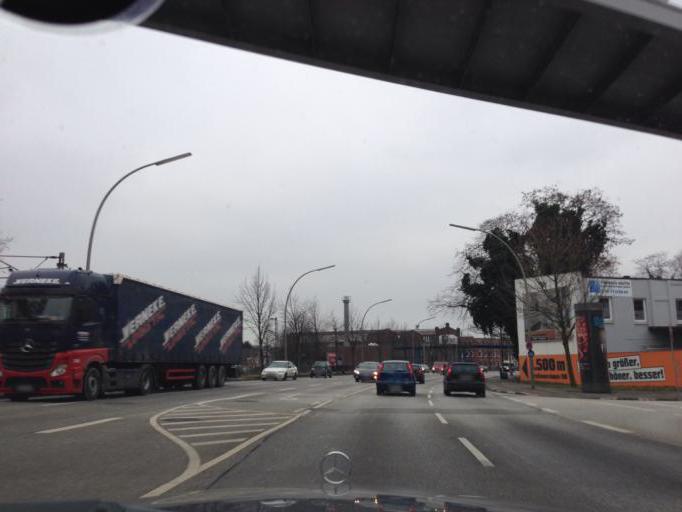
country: DE
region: Hamburg
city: Harburg
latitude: 53.4626
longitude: 9.9848
